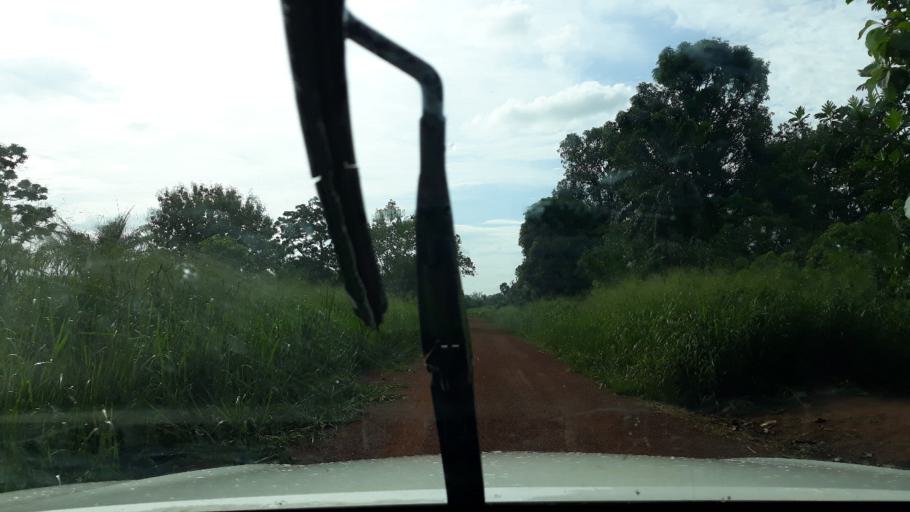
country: CD
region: Equateur
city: Libenge
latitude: 3.7357
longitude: 18.7571
